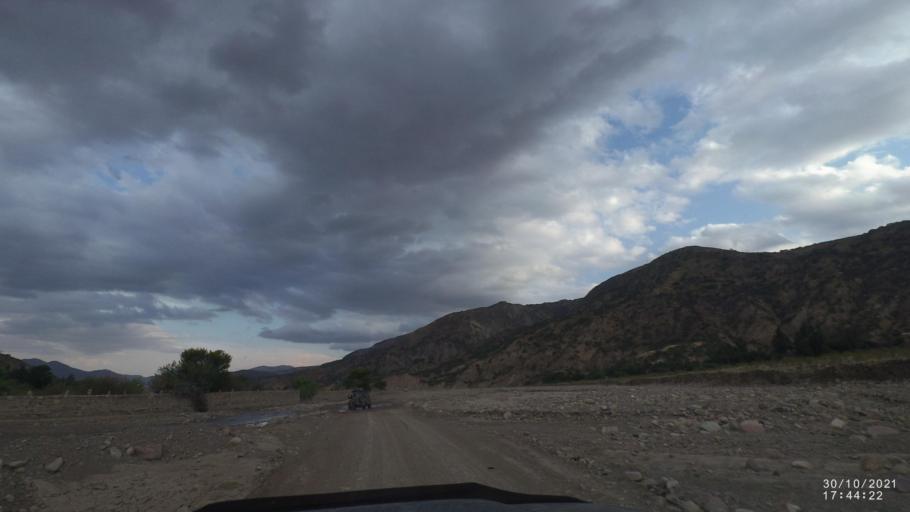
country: BO
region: Cochabamba
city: Sipe Sipe
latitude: -17.5277
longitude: -66.5345
